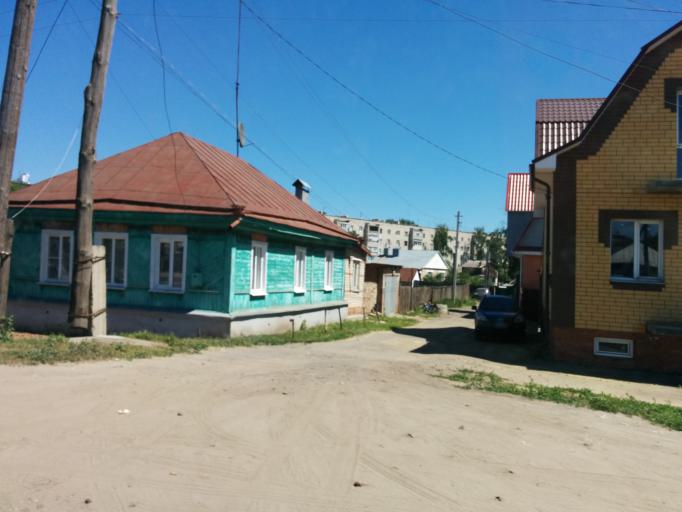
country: RU
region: Tambov
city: Morshansk
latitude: 53.4369
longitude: 41.8014
